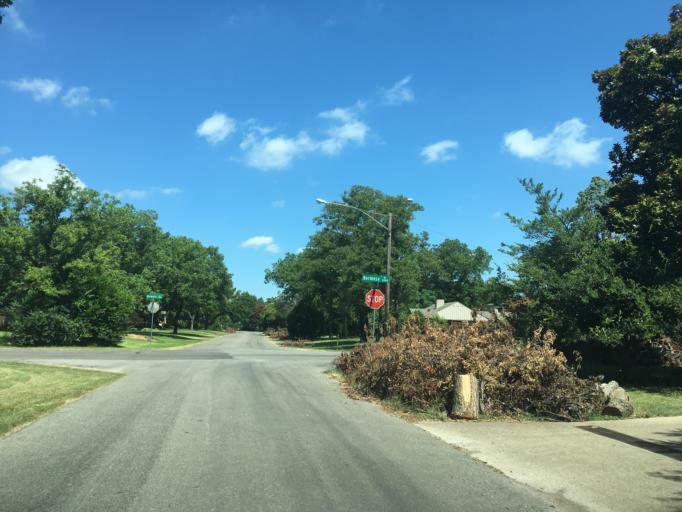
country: US
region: Texas
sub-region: Dallas County
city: Garland
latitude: 32.8326
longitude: -96.6926
